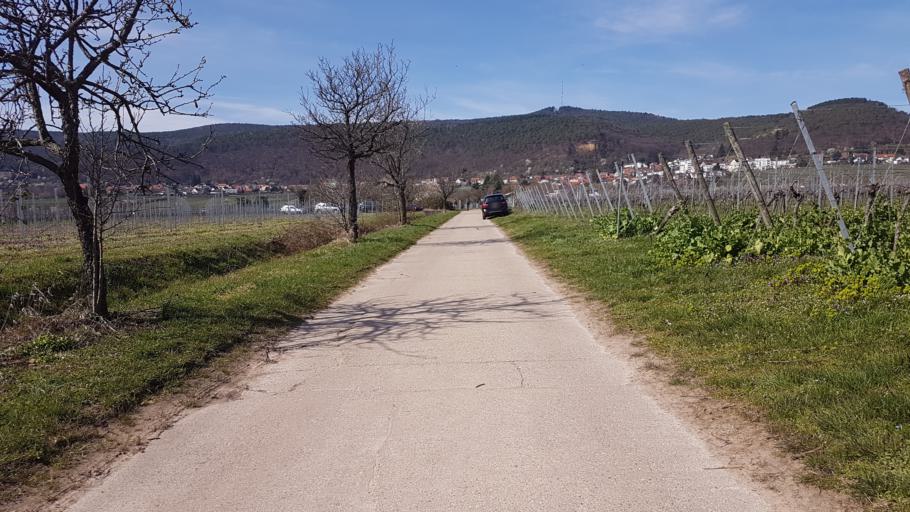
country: DE
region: Rheinland-Pfalz
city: Neustadt
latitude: 49.3656
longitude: 8.1567
